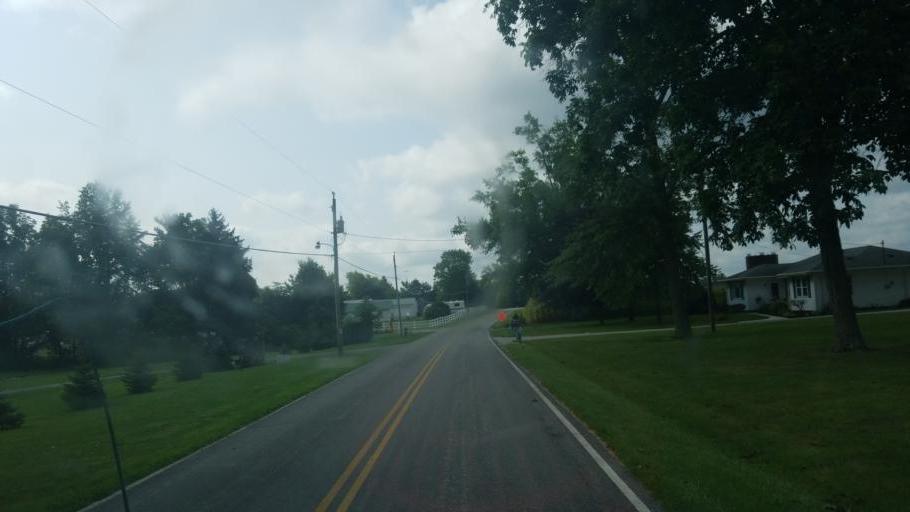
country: US
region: Ohio
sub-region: Morrow County
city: Cardington
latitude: 40.5692
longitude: -82.9958
